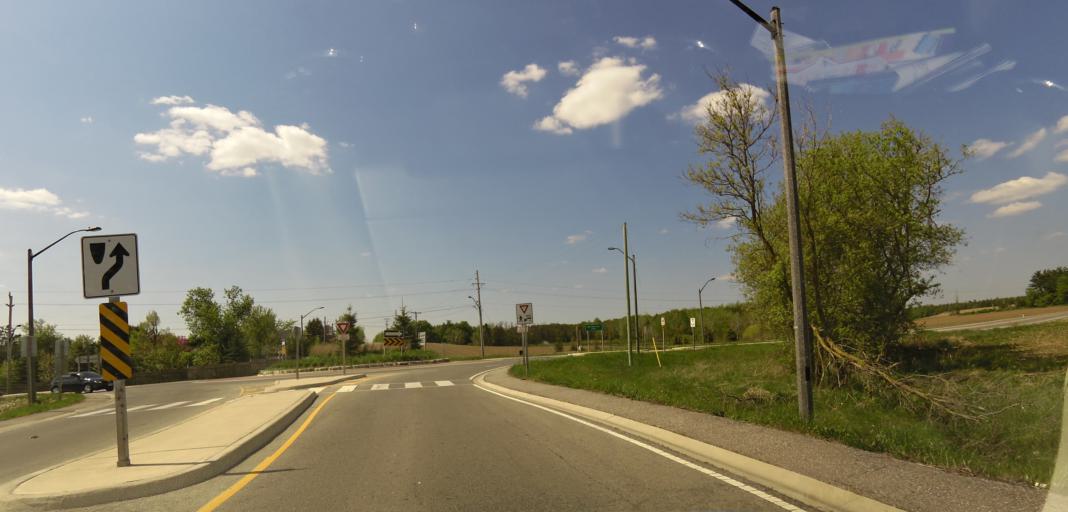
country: CA
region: Ontario
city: Brampton
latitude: 43.8295
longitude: -79.8826
